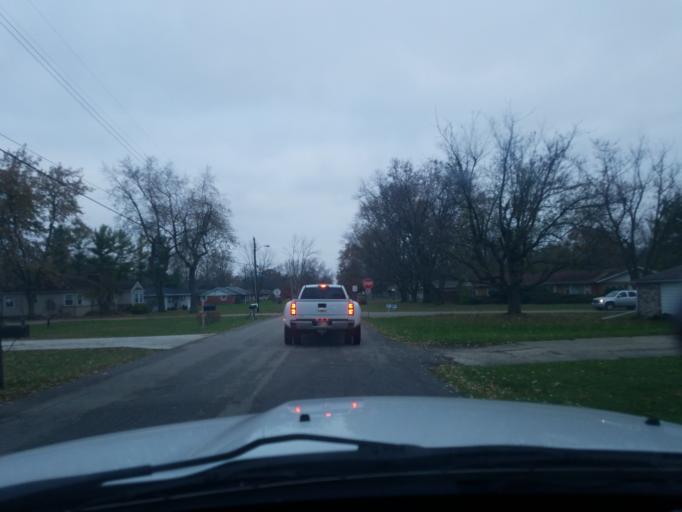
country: US
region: Indiana
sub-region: Delaware County
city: Muncie
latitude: 40.2276
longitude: -85.4058
